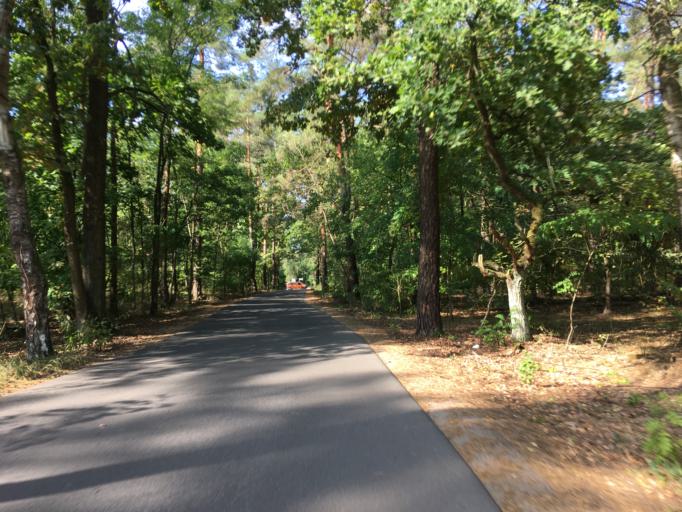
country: DE
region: Berlin
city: Rahnsdorf
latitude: 52.4233
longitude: 13.6826
